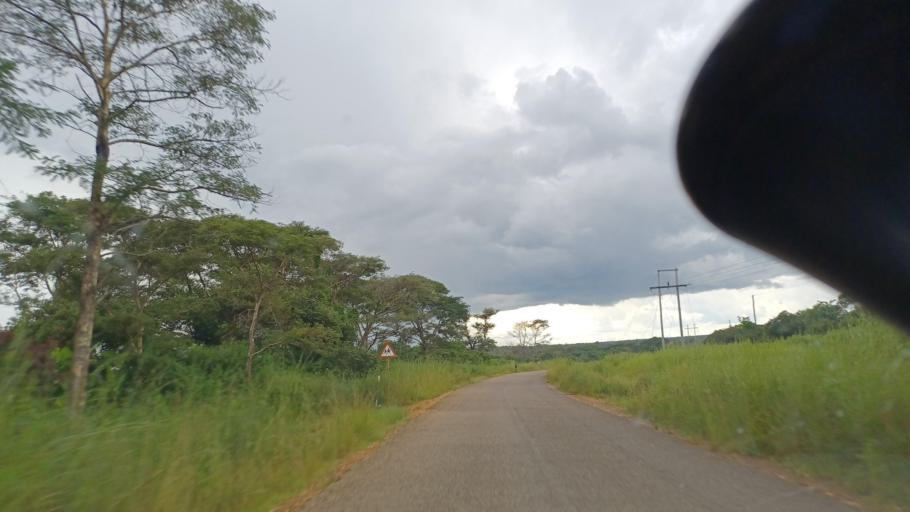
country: ZM
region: North-Western
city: Kasempa
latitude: -13.0090
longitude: 26.0078
